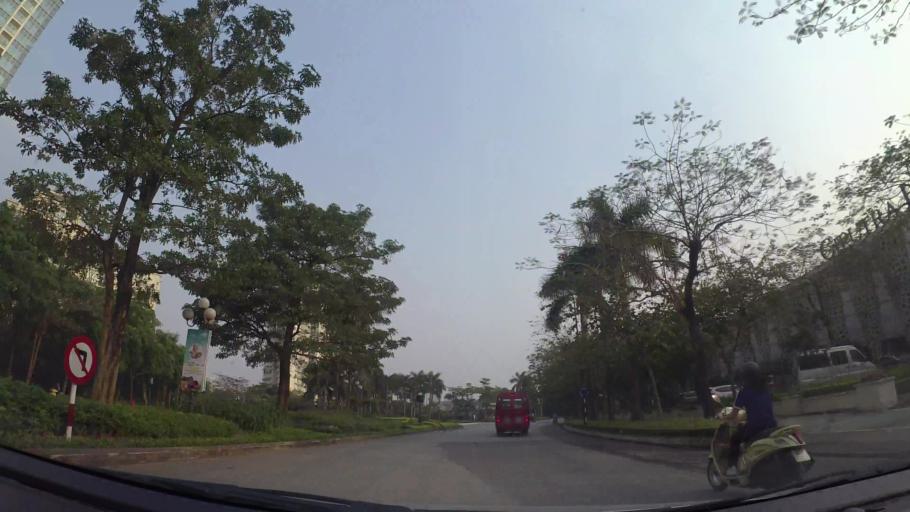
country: VN
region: Ha Noi
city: Tay Ho
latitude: 21.0797
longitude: 105.7911
